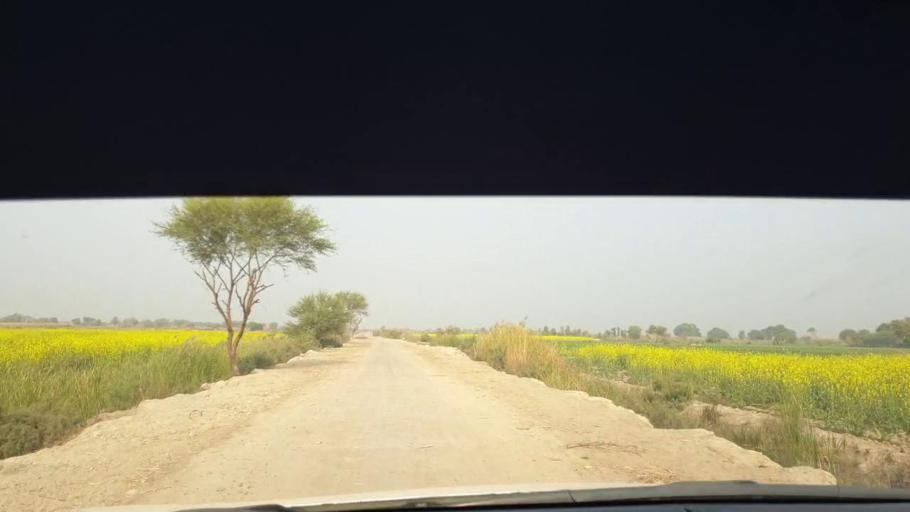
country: PK
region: Sindh
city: Berani
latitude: 25.8390
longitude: 68.8476
